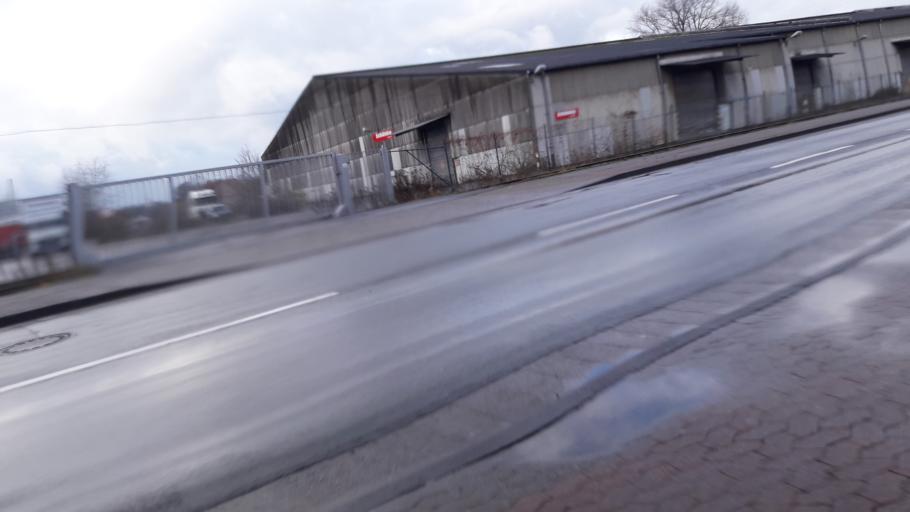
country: DE
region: North Rhine-Westphalia
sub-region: Regierungsbezirk Detmold
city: Minden
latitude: 52.3010
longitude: 8.9346
